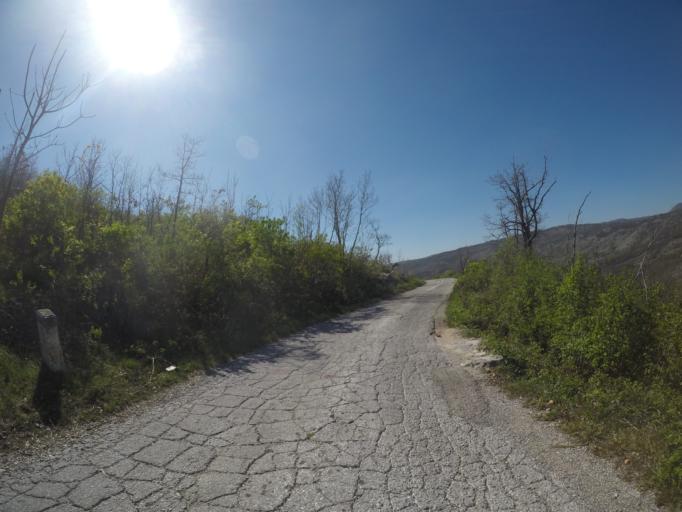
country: ME
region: Danilovgrad
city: Danilovgrad
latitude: 42.5352
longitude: 19.0161
